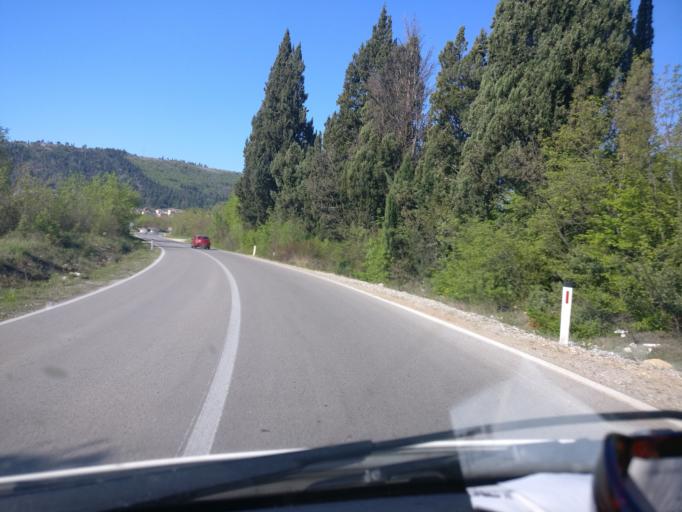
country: BA
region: Federation of Bosnia and Herzegovina
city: Tasovcici
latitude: 43.1230
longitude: 17.7494
